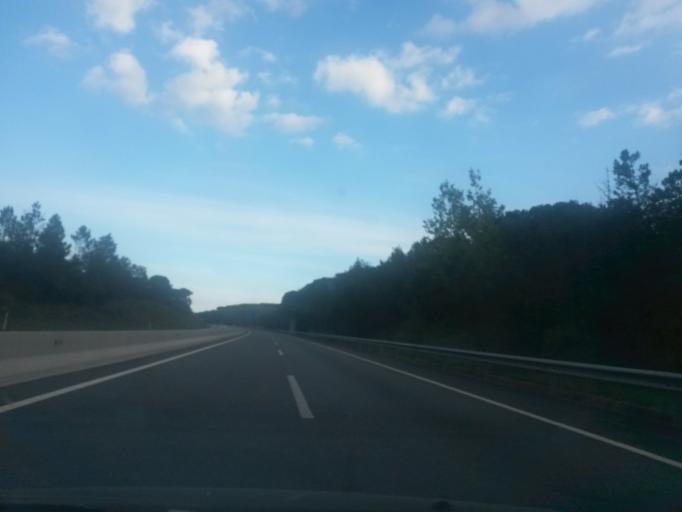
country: ES
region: Catalonia
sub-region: Provincia de Girona
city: Vilobi d'Onyar
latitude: 41.8768
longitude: 2.7414
